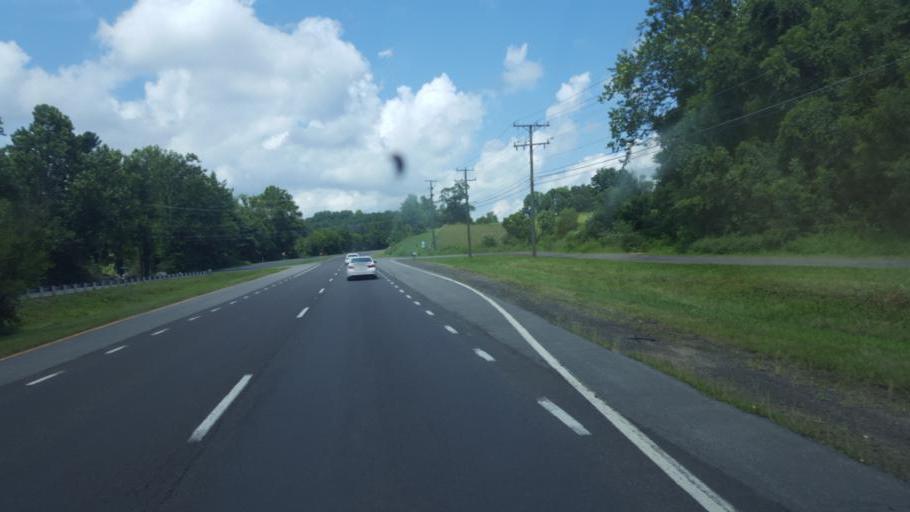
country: US
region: Virginia
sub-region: Fauquier County
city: Warrenton
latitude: 38.7774
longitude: -77.8246
